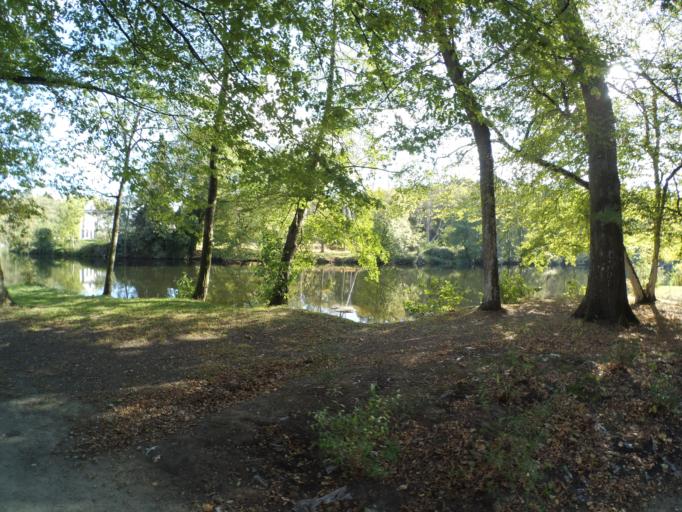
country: FR
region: Pays de la Loire
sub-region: Departement de la Loire-Atlantique
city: Clisson
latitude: 47.0844
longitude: -1.2715
